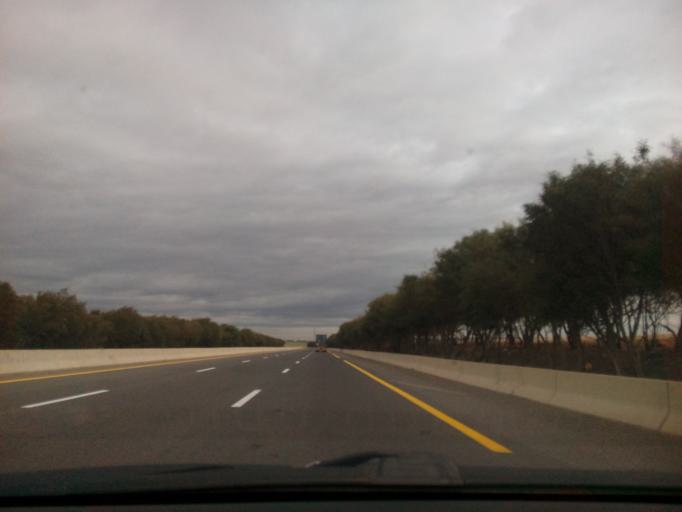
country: DZ
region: Sidi Bel Abbes
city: Sidi Bel Abbes
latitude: 35.2324
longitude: -0.6361
